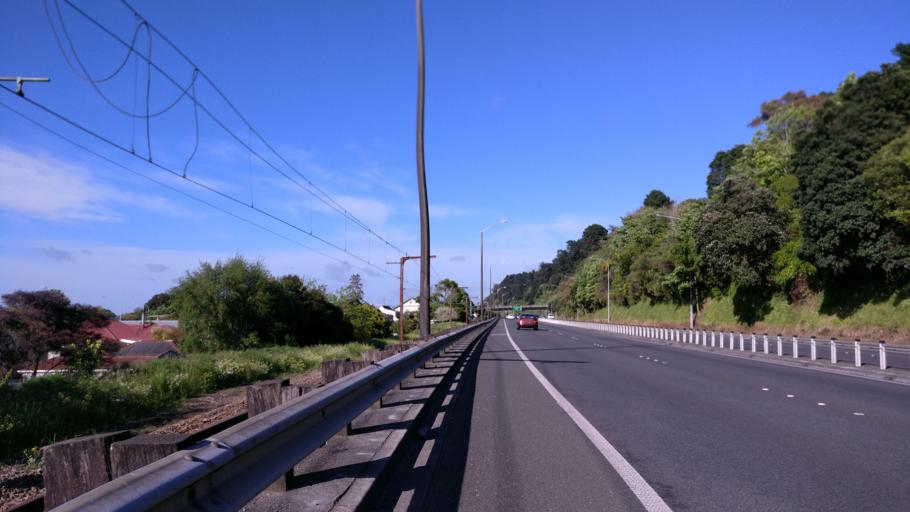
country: NZ
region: Wellington
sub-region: Lower Hutt City
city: Lower Hutt
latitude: -41.2073
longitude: 174.8981
